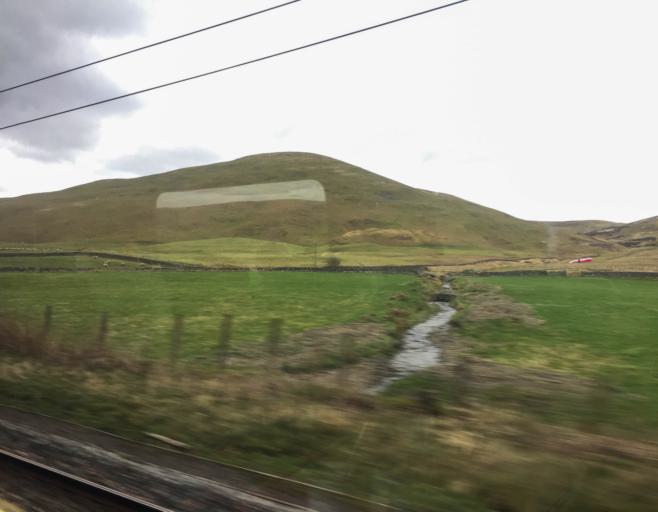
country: GB
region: Scotland
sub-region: South Lanarkshire
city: Douglas
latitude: 55.4943
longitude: -3.6849
